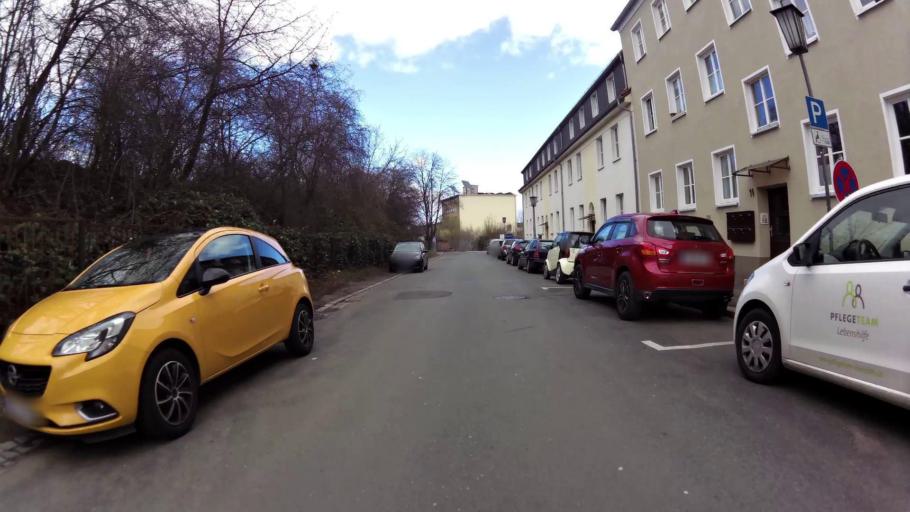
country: DE
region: Thuringia
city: Weimar
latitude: 50.9903
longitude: 11.3334
